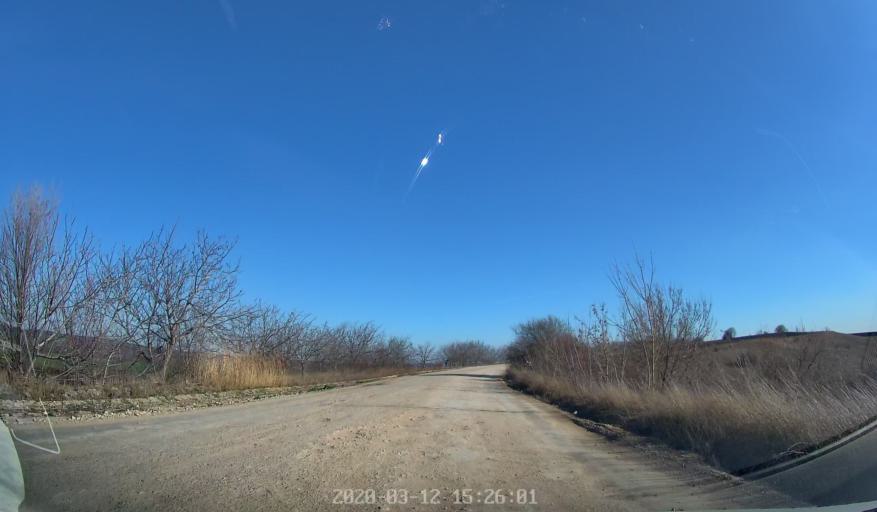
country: MD
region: Chisinau
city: Ciorescu
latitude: 47.1802
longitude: 28.9216
